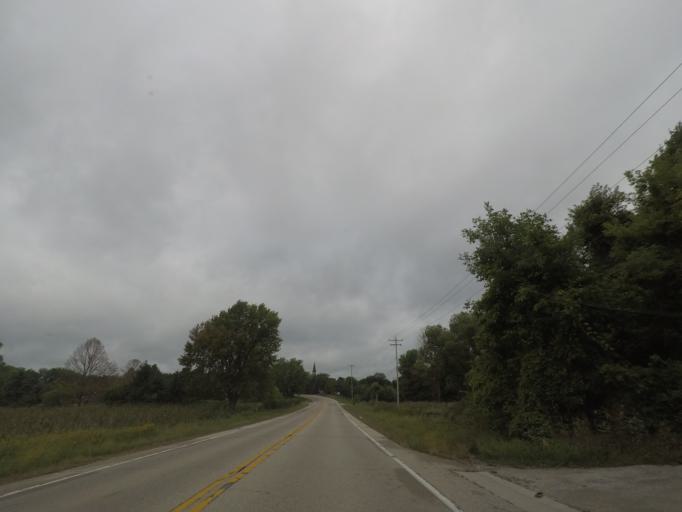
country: US
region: Wisconsin
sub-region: Waukesha County
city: Dousman
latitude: 43.0195
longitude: -88.5751
